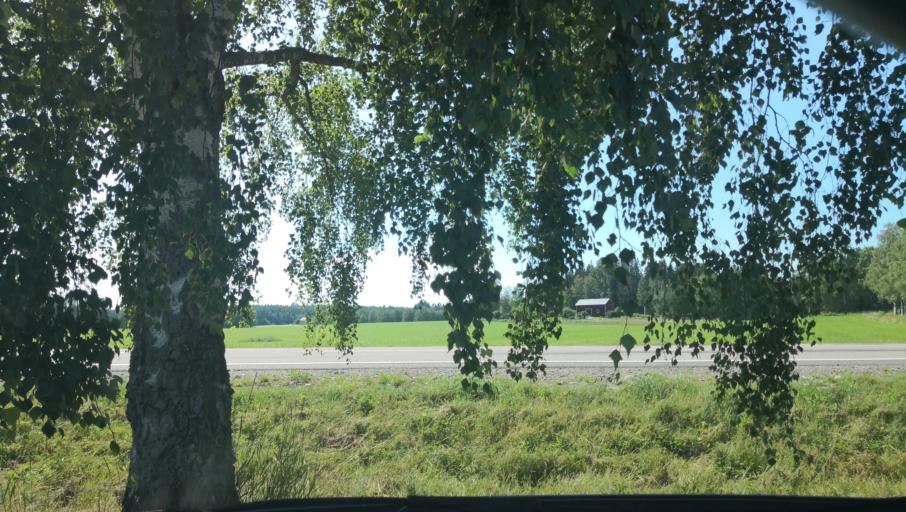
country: SE
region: Gaevleborg
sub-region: Bollnas Kommun
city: Kilafors
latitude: 61.2283
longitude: 16.5601
